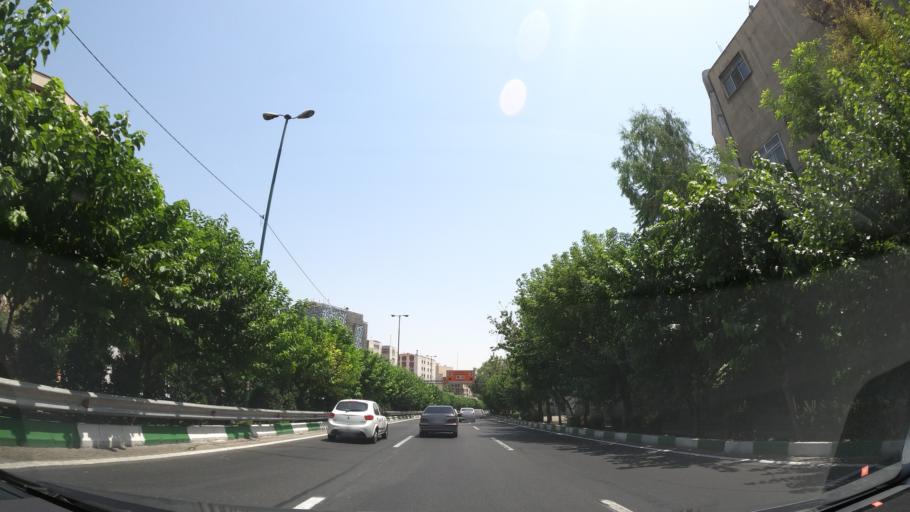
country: IR
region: Tehran
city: Tehran
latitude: 35.7274
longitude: 51.4232
